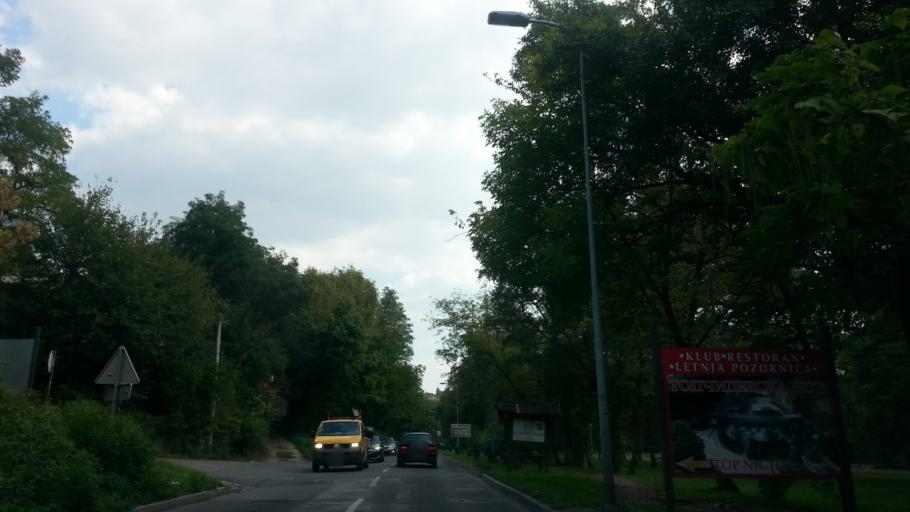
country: RS
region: Central Serbia
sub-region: Belgrade
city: Savski Venac
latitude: 44.7837
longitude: 20.4376
